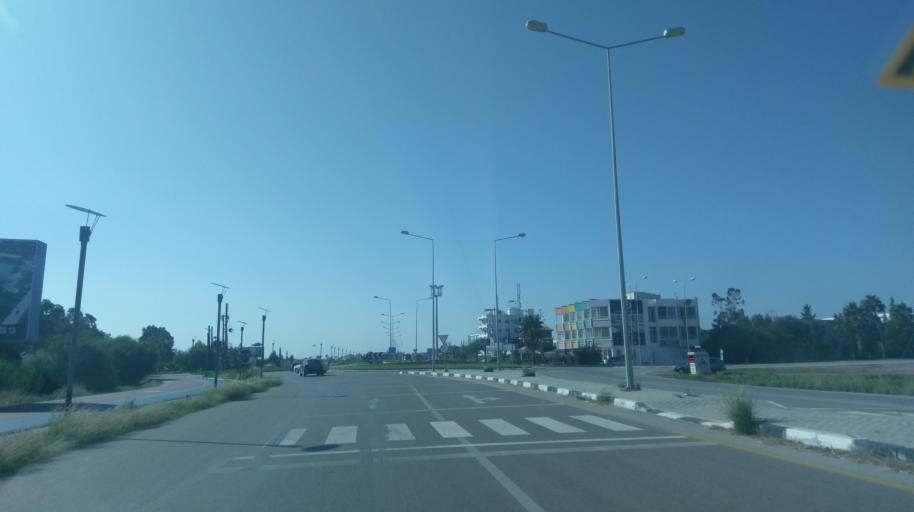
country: CY
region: Ammochostos
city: Trikomo
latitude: 35.2614
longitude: 33.9100
